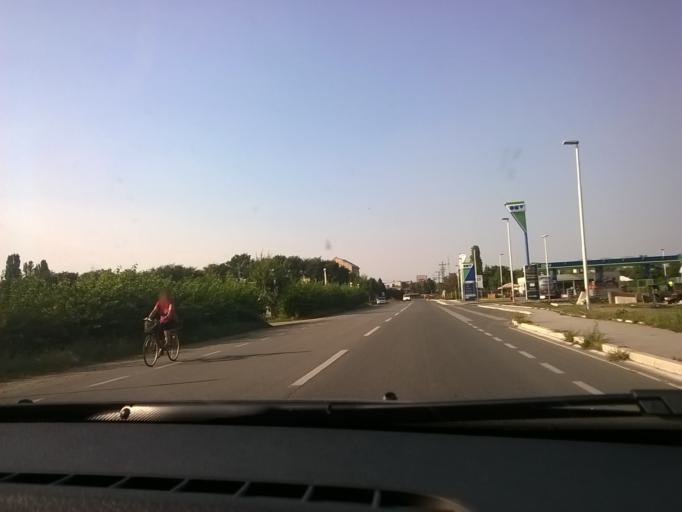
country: RS
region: Autonomna Pokrajina Vojvodina
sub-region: Juznobanatski Okrug
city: Vrsac
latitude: 45.1313
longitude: 21.2875
